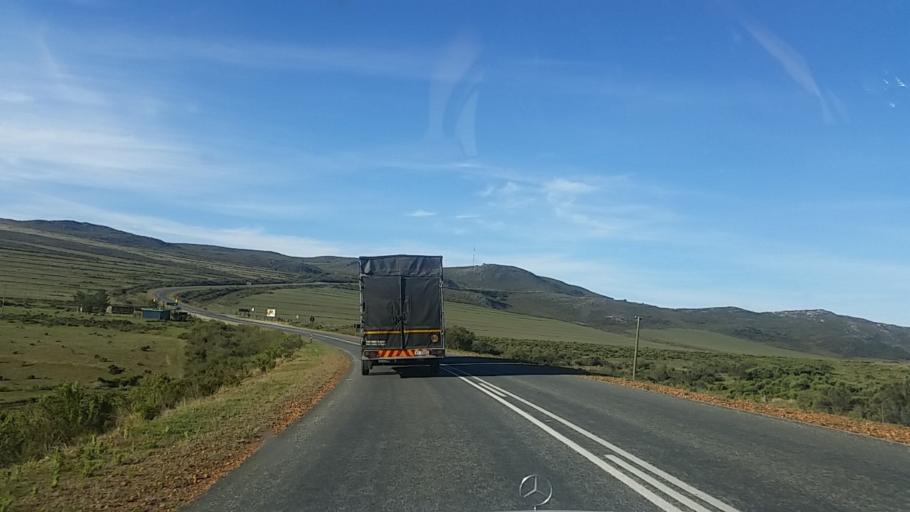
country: ZA
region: Western Cape
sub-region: Eden District Municipality
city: Knysna
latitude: -33.7387
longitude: 23.0390
